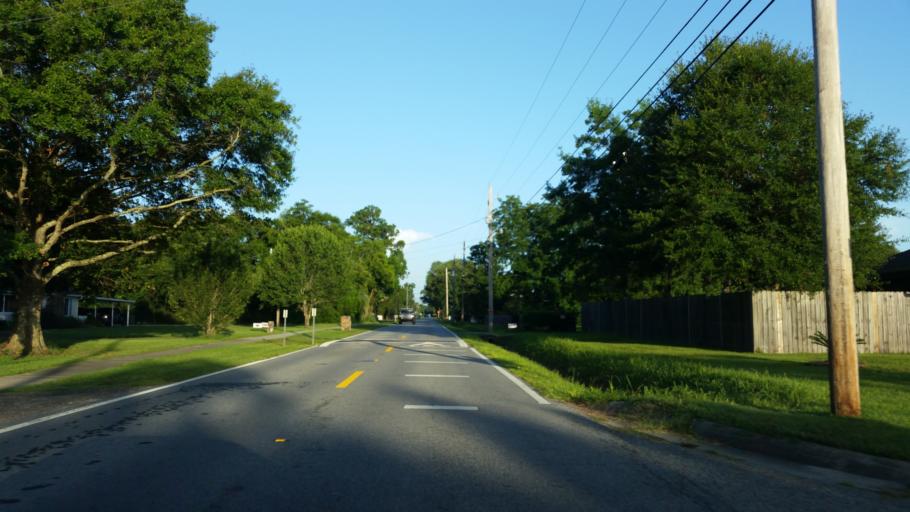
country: US
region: Florida
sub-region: Escambia County
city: Bellview
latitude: 30.4688
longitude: -87.3187
